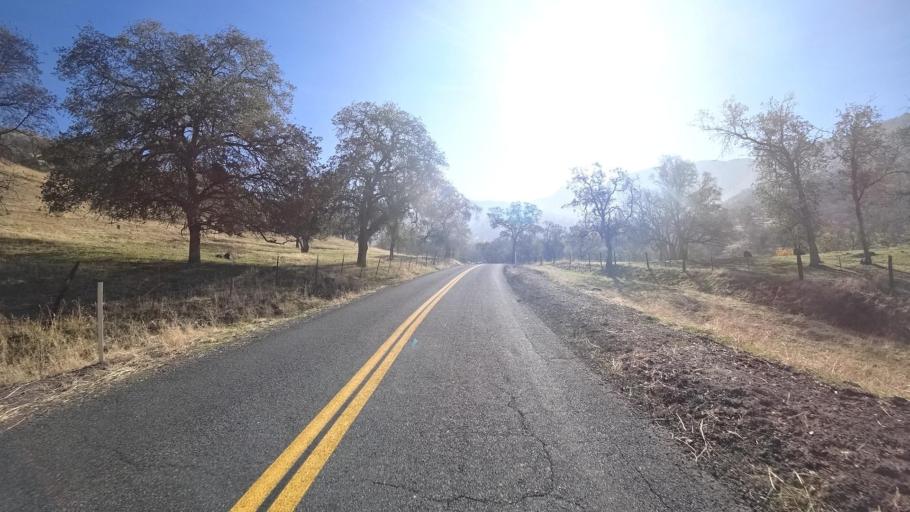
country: US
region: California
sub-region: Kern County
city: Alta Sierra
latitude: 35.7889
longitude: -118.7926
